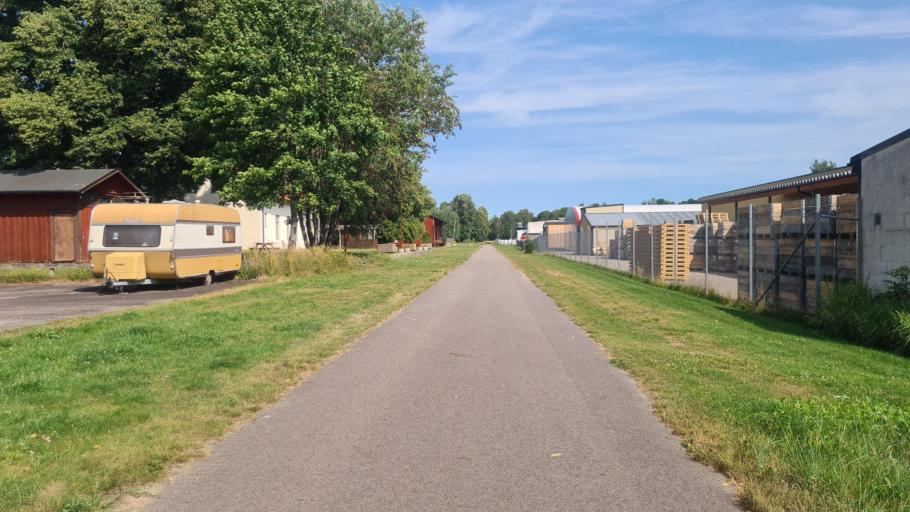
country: SE
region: Kronoberg
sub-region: Ljungby Kommun
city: Lagan
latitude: 56.9131
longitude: 13.9898
